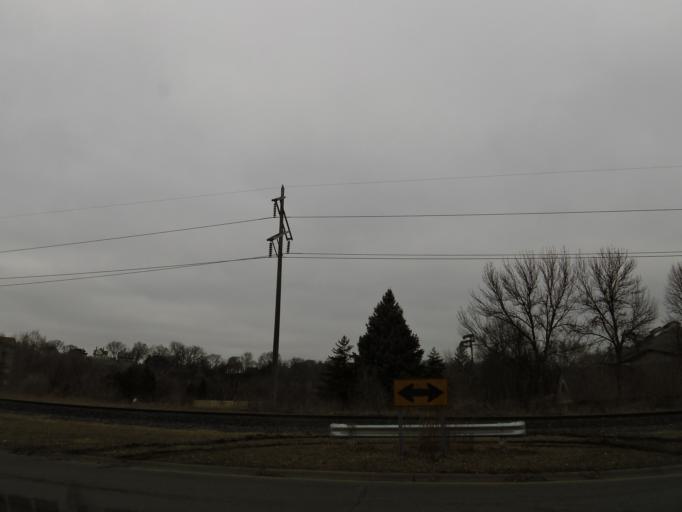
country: US
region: Minnesota
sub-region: Dakota County
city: West Saint Paul
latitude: 44.9323
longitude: -93.1245
